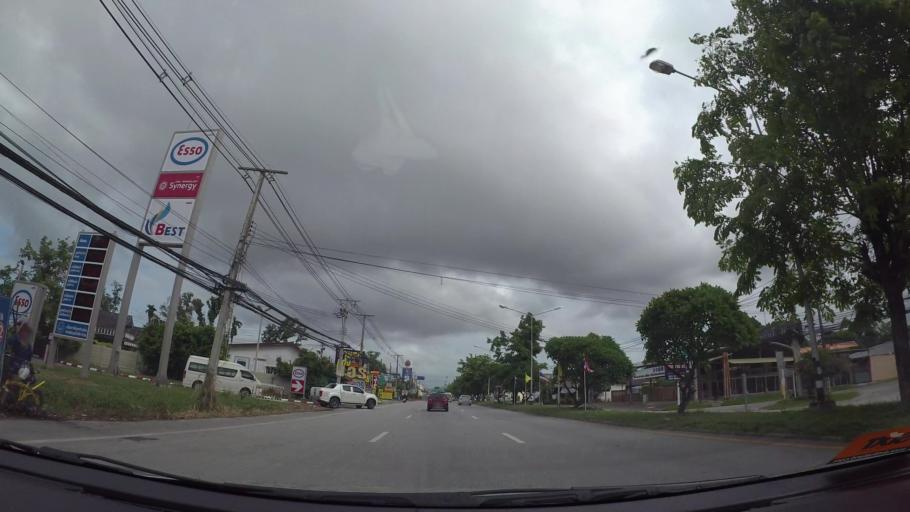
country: TH
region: Rayong
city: Rayong
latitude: 12.6873
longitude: 101.2120
